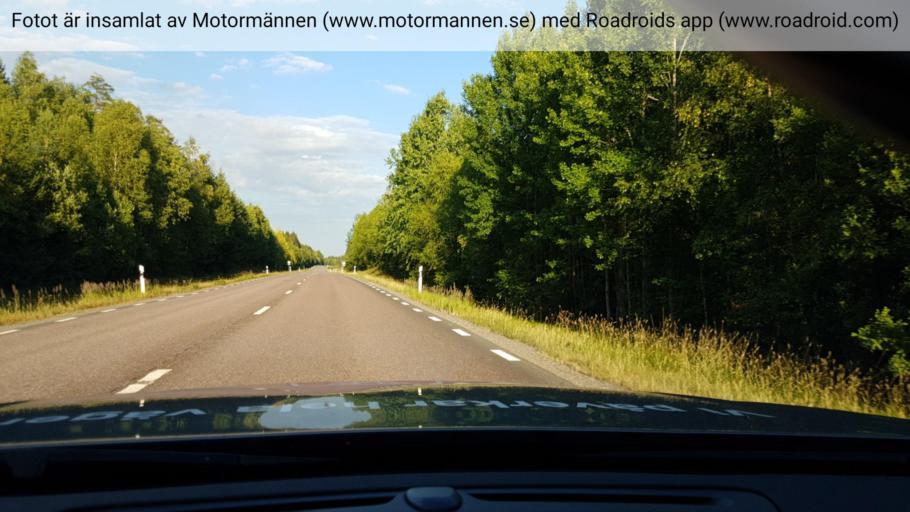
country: SE
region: Uppsala
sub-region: Enkopings Kommun
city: Orsundsbro
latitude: 59.8838
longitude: 17.2148
